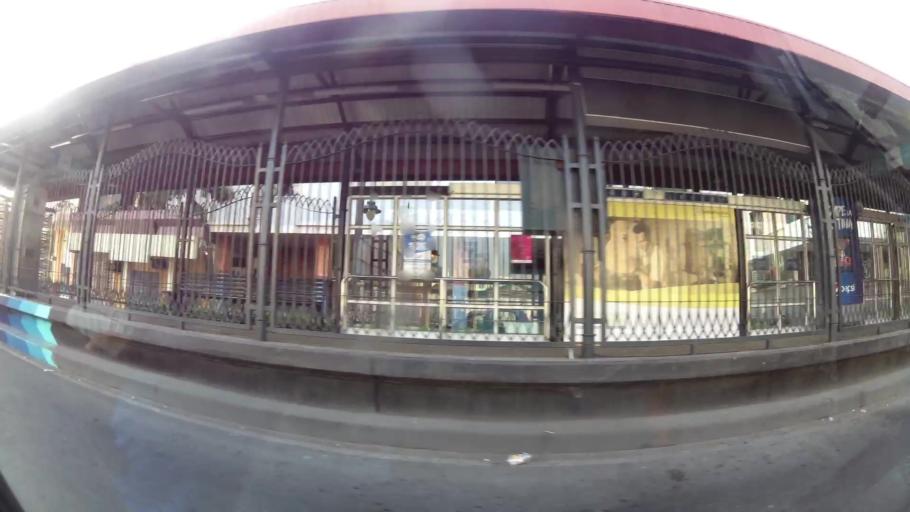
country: EC
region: Guayas
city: Eloy Alfaro
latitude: -2.1872
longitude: -79.8793
